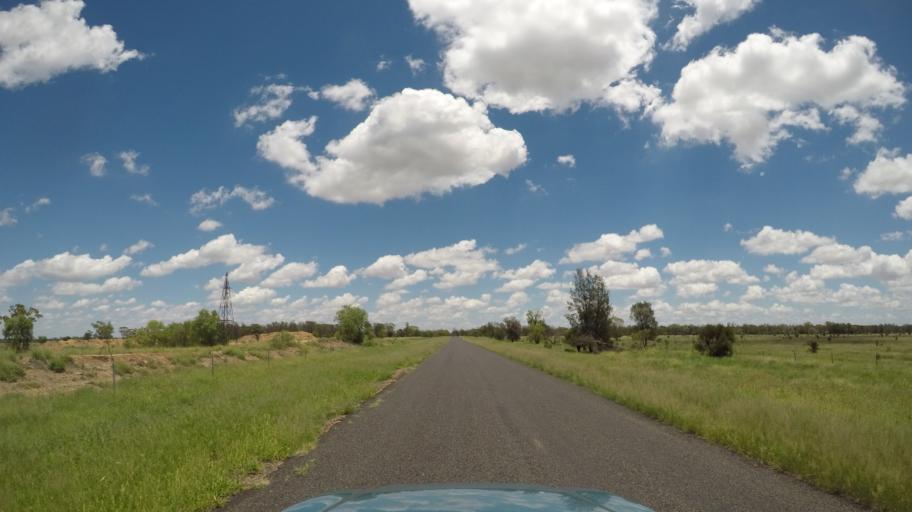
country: AU
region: Queensland
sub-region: Goondiwindi
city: Goondiwindi
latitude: -28.1601
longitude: 150.1303
